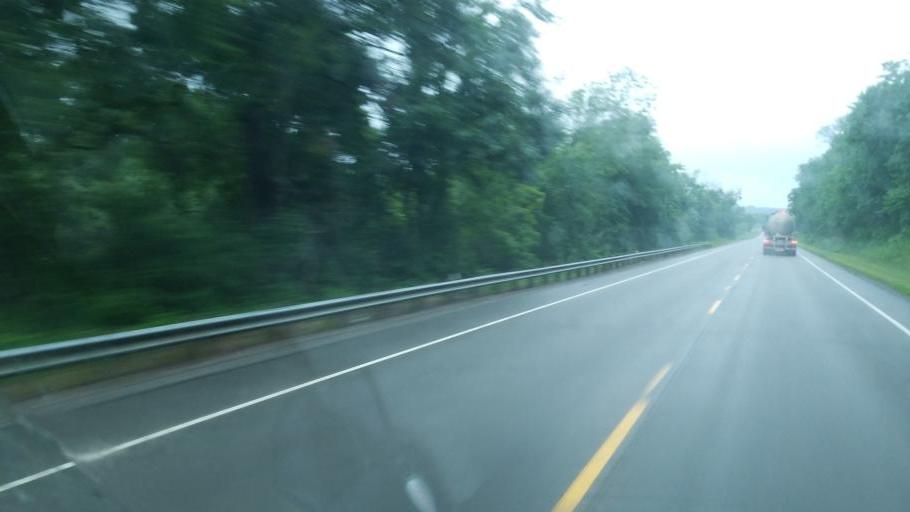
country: US
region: Ohio
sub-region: Coshocton County
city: Coshocton
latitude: 40.2866
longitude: -81.8806
